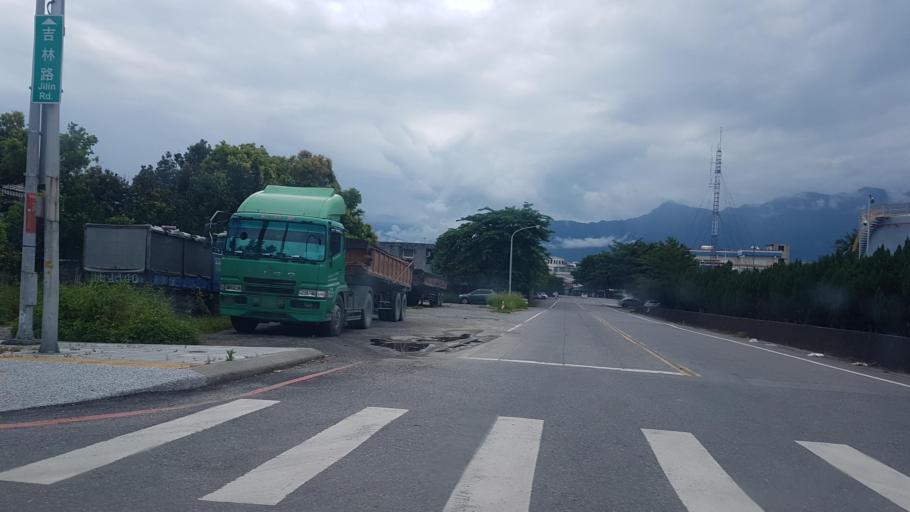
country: TW
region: Taiwan
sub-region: Hualien
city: Hualian
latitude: 23.9974
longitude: 121.6331
